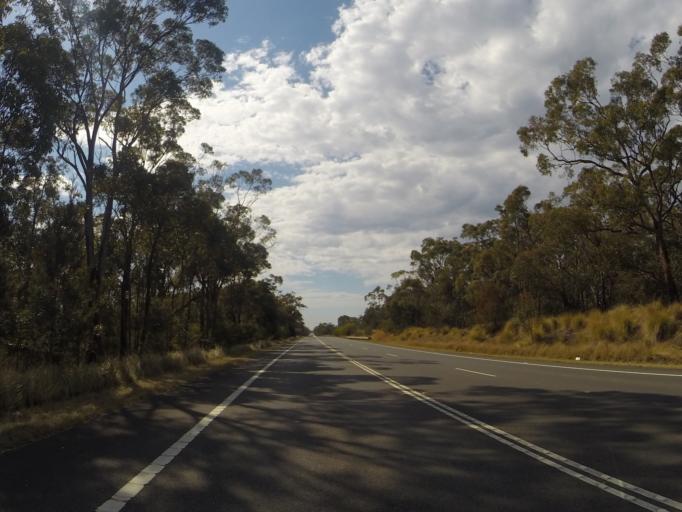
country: AU
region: New South Wales
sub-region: Liverpool
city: Holsworthy
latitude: -34.0288
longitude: 150.9643
